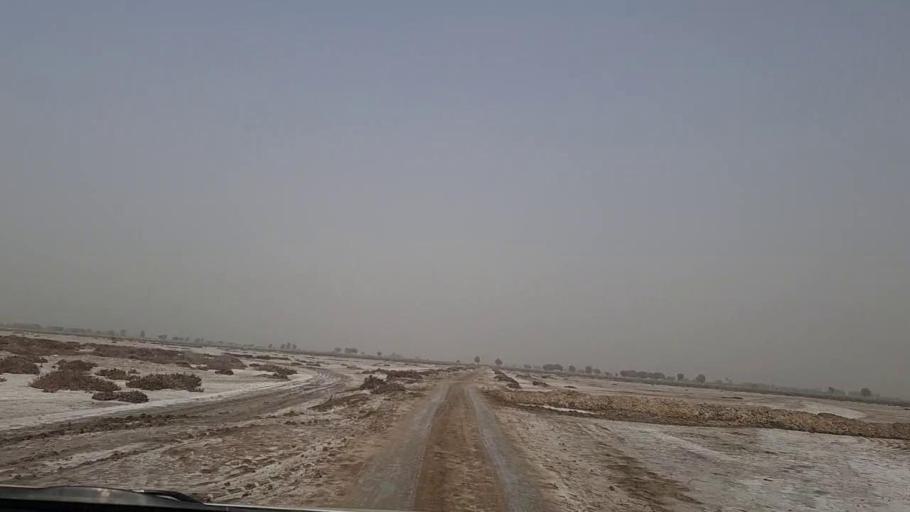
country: PK
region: Sindh
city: Pithoro
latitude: 25.4669
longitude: 69.2665
